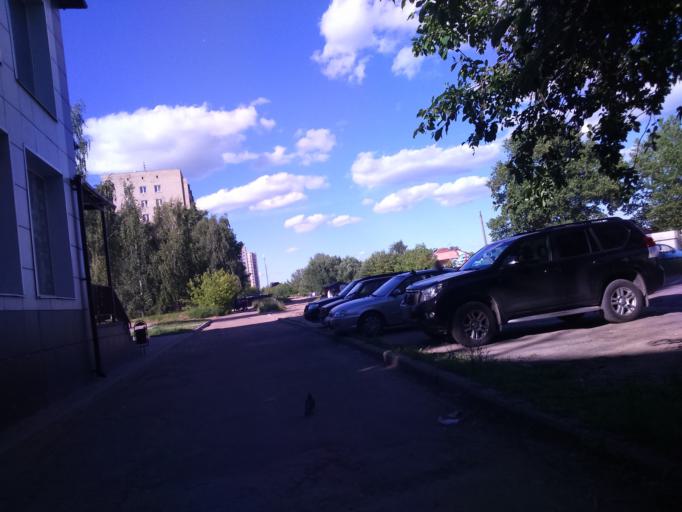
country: RU
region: Jaroslavl
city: Yaroslavl
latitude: 57.5746
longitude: 39.8627
